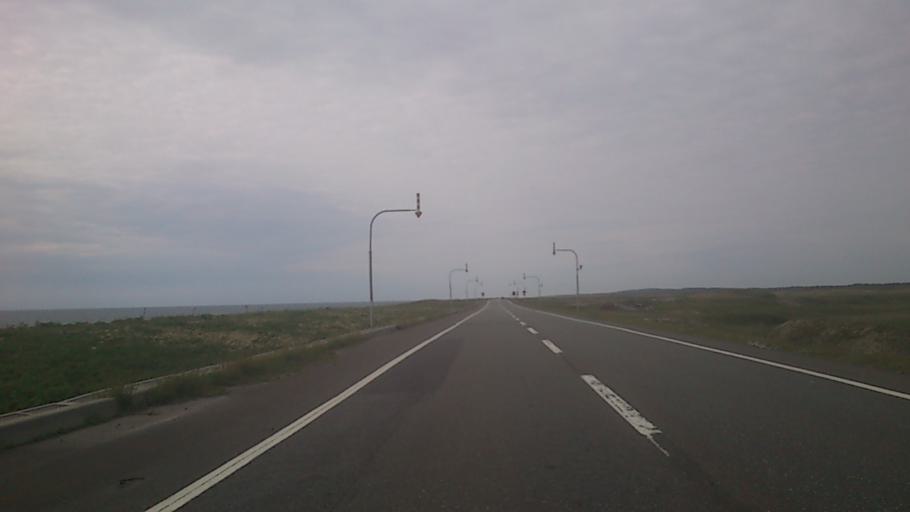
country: JP
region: Hokkaido
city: Makubetsu
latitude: 45.0288
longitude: 141.6661
